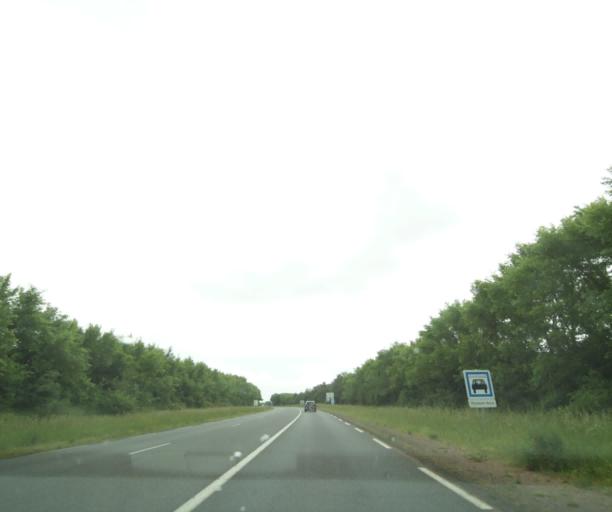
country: FR
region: Poitou-Charentes
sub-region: Departement des Deux-Sevres
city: Airvault
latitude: 46.8174
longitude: -0.2064
